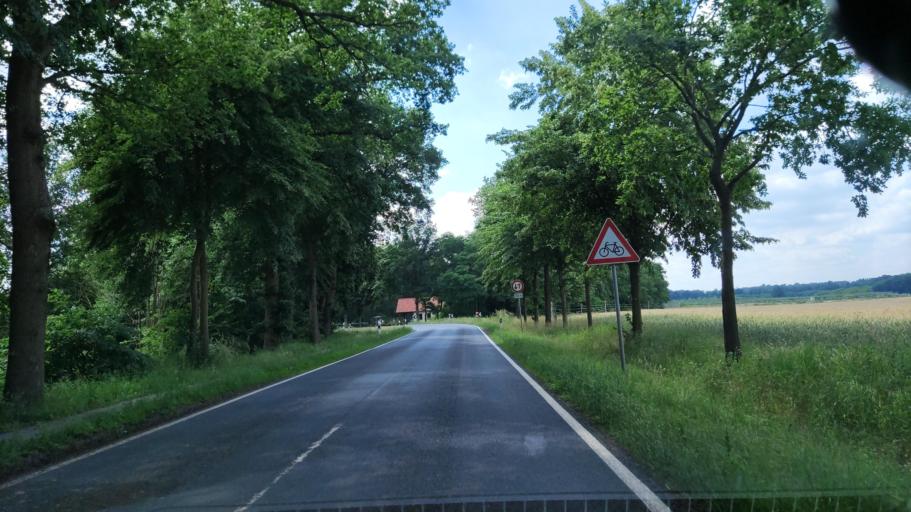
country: DE
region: Mecklenburg-Vorpommern
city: Lubtheen
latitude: 53.3359
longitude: 11.1318
